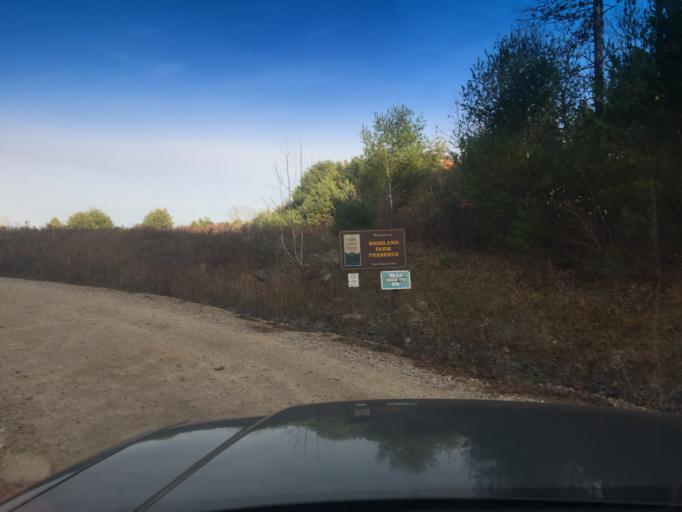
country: US
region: Maine
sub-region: York County
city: York Harbor
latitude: 43.1710
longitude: -70.7165
